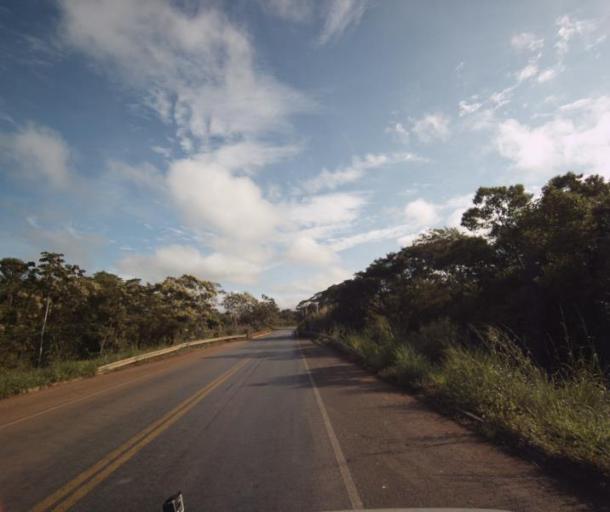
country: BR
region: Goias
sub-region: Padre Bernardo
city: Padre Bernardo
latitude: -15.4899
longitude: -48.6185
